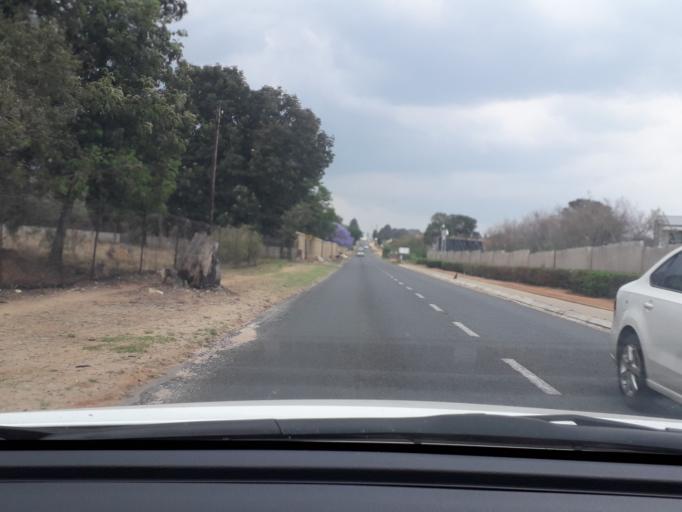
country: ZA
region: Gauteng
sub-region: West Rand District Municipality
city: Muldersdriseloop
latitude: -26.0631
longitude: 27.9256
